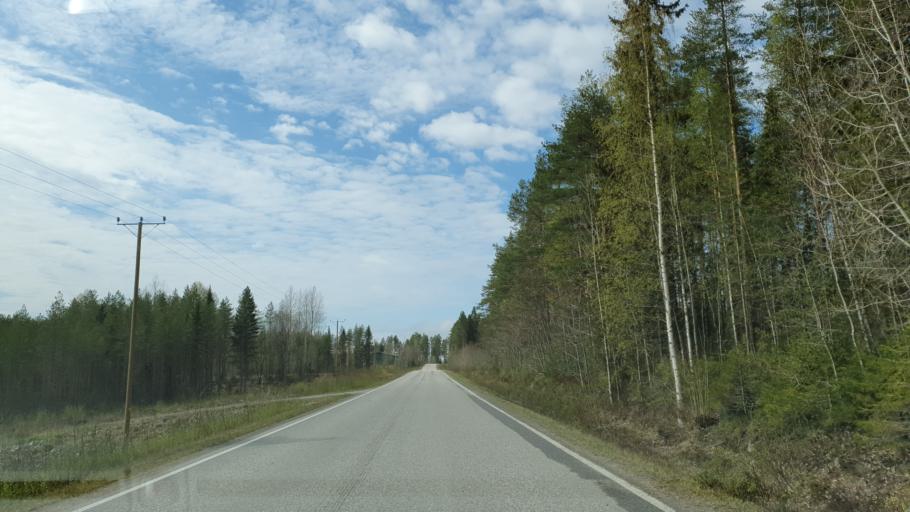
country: FI
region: Kainuu
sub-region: Kehys-Kainuu
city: Kuhmo
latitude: 64.1214
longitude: 29.6766
